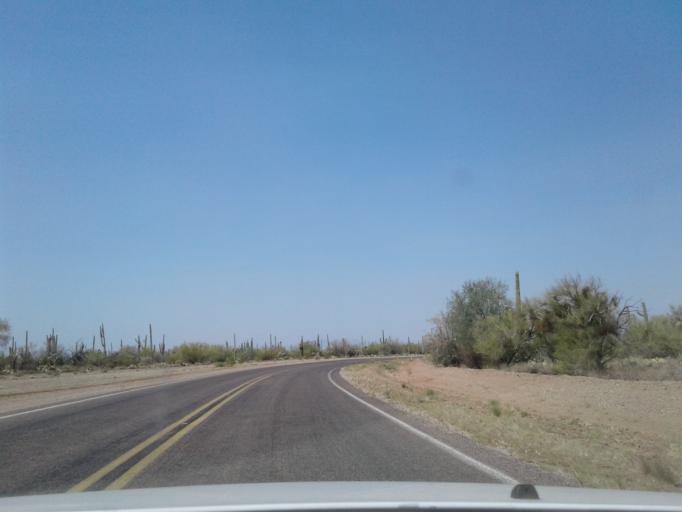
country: US
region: Arizona
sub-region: Pima County
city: Marana
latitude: 32.6279
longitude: -111.1746
